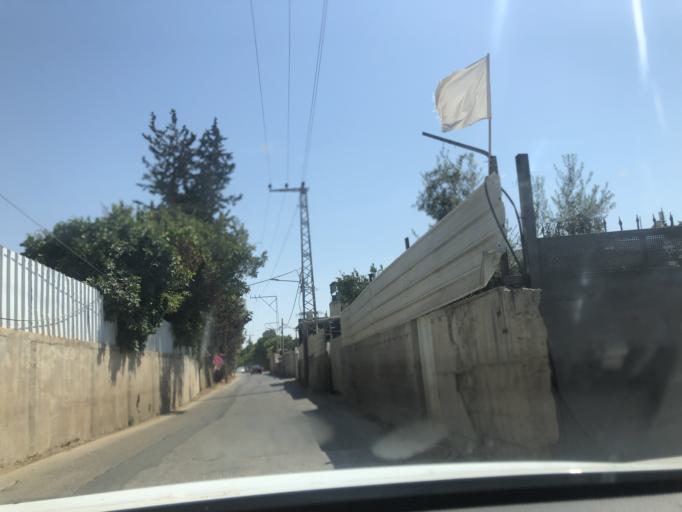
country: IL
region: Central District
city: Lod
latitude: 31.9541
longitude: 34.8807
